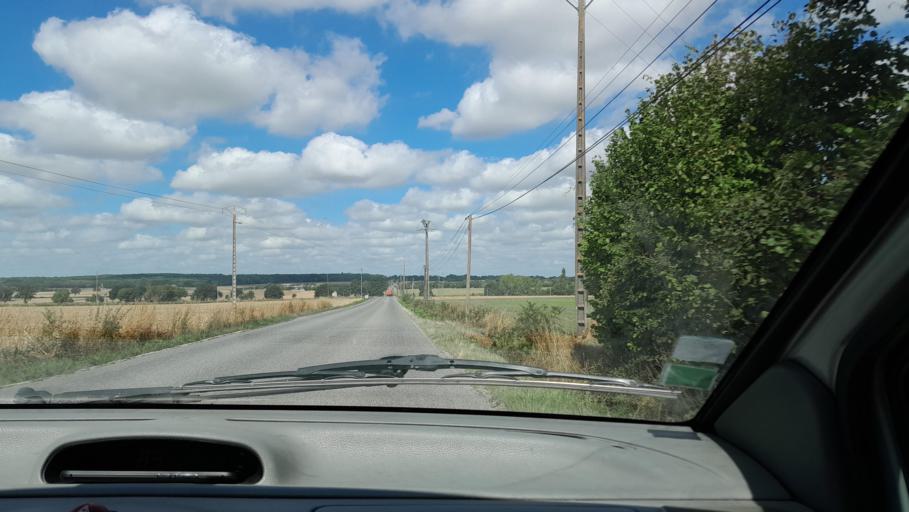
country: FR
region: Pays de la Loire
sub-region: Departement de la Mayenne
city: Ballots
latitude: 47.8710
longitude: -1.0001
